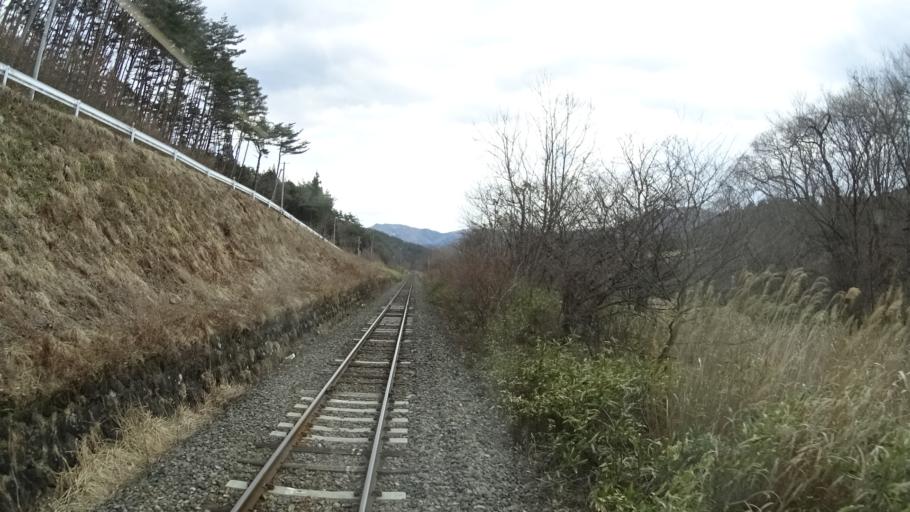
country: JP
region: Iwate
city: Tono
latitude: 39.3200
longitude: 141.3676
